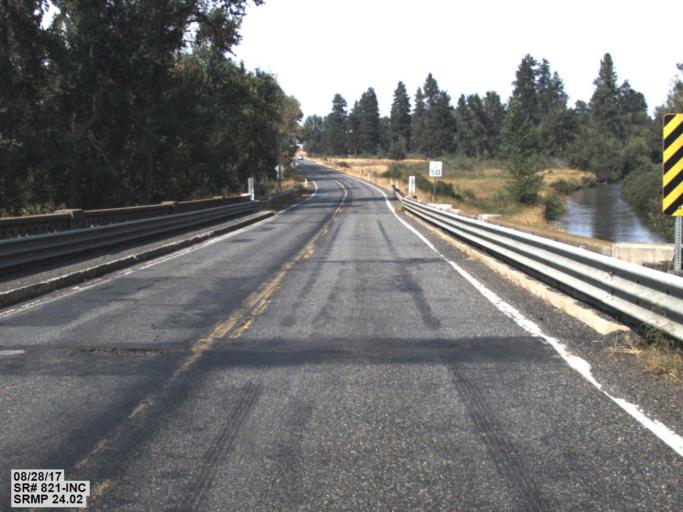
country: US
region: Washington
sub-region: Kittitas County
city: Ellensburg
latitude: 46.9173
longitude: -120.5081
